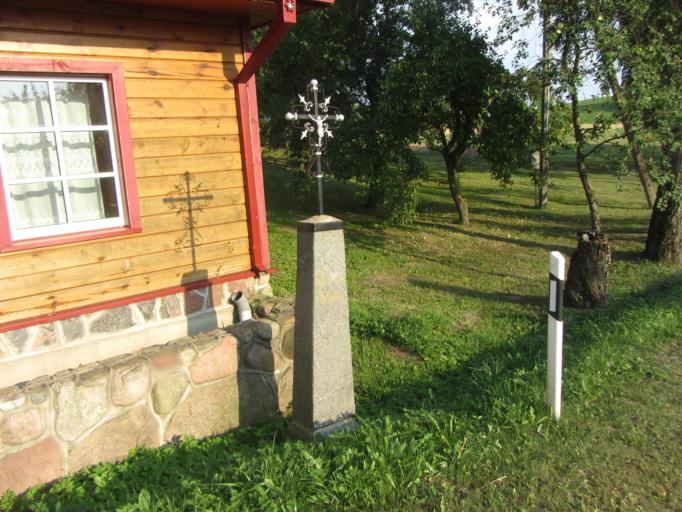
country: LT
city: Lazdijai
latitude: 54.1999
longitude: 23.5114
